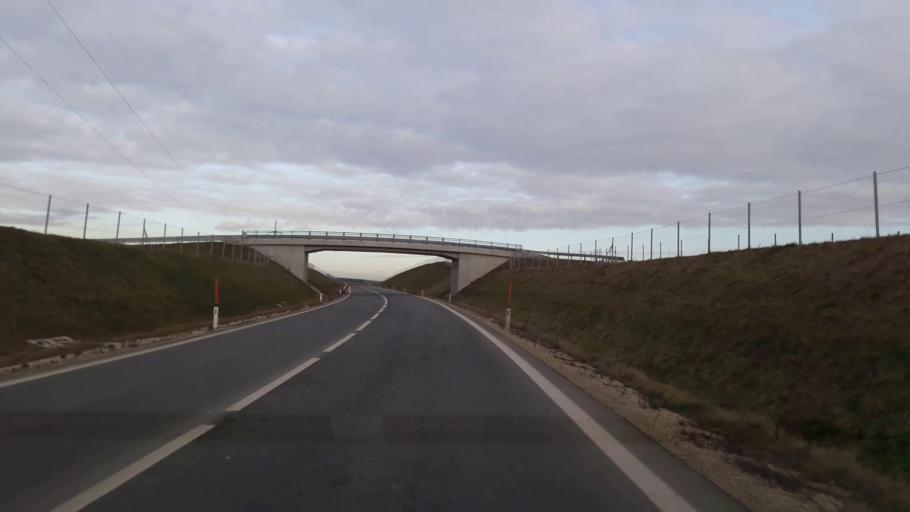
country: AT
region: Lower Austria
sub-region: Politischer Bezirk Mistelbach
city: Mistelbach
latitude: 48.5644
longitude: 16.5546
